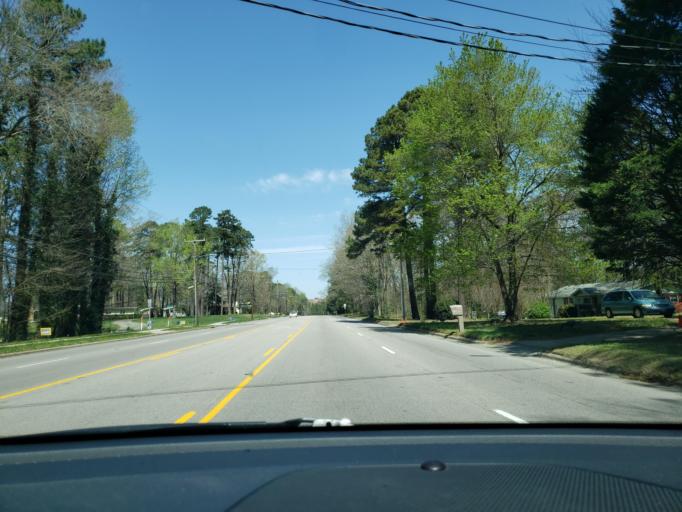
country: US
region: North Carolina
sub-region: Durham County
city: Durham
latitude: 35.9591
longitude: -78.8930
